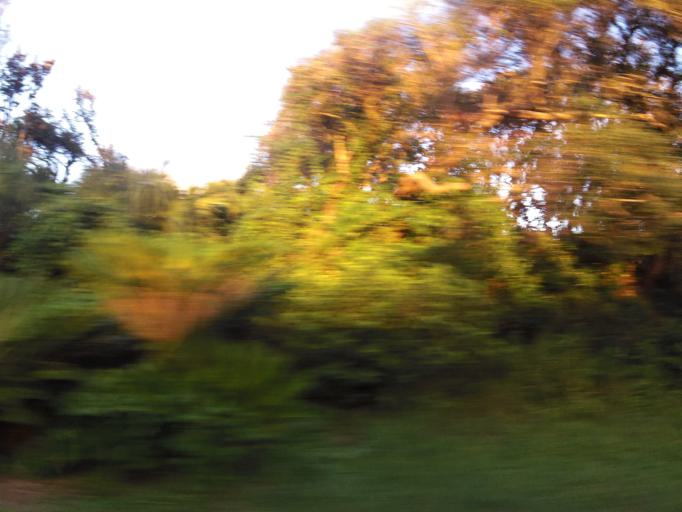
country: US
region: Florida
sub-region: Saint Johns County
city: Sawgrass
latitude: 30.1760
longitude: -81.3608
